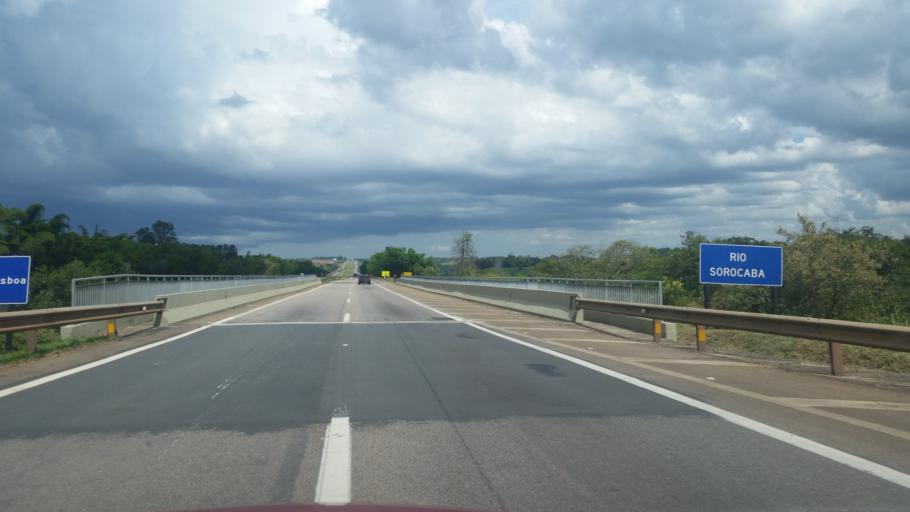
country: BR
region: Sao Paulo
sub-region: Boituva
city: Boituva
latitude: -23.2859
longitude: -47.7706
